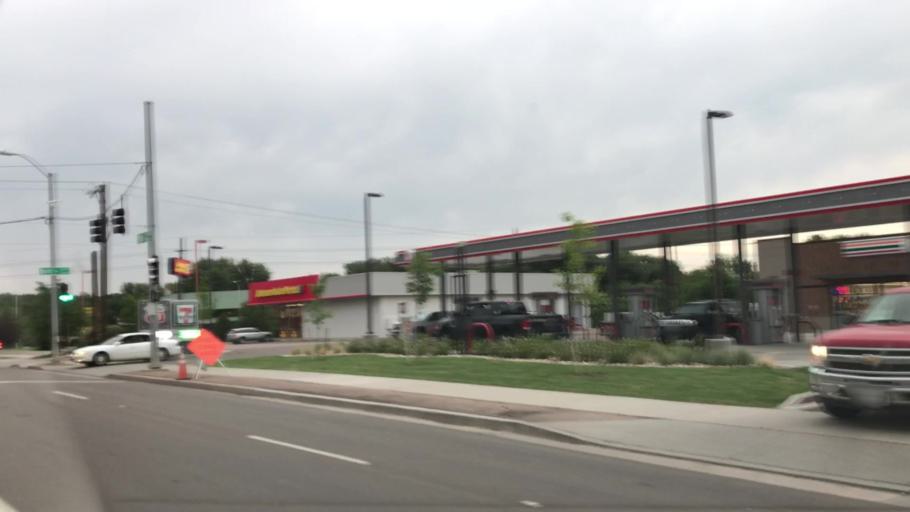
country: US
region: Colorado
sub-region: El Paso County
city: Colorado Springs
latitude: 38.8389
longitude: -104.8591
